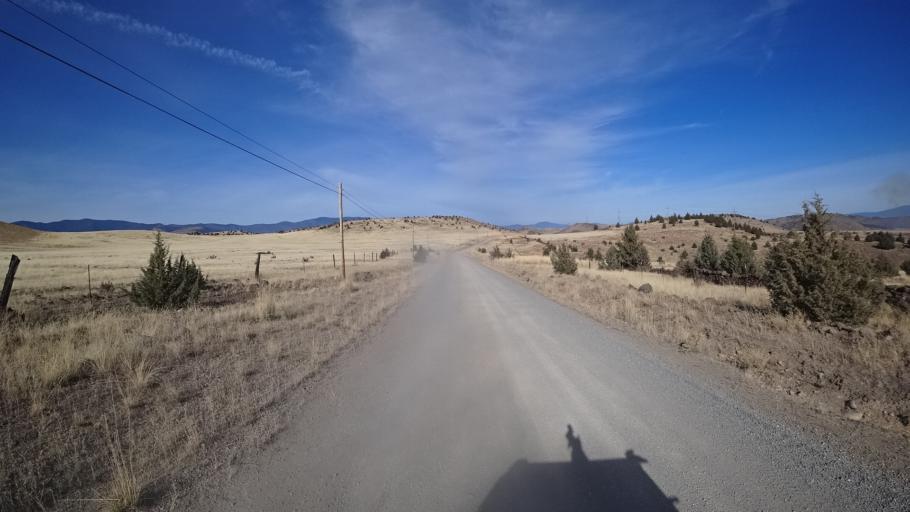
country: US
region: California
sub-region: Siskiyou County
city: Weed
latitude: 41.4935
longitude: -122.4530
